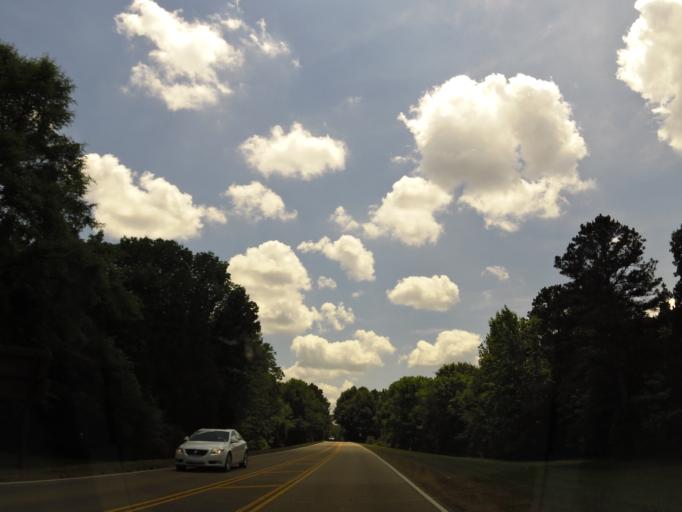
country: US
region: Mississippi
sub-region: Lee County
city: Tupelo
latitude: 34.2963
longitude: -88.7263
